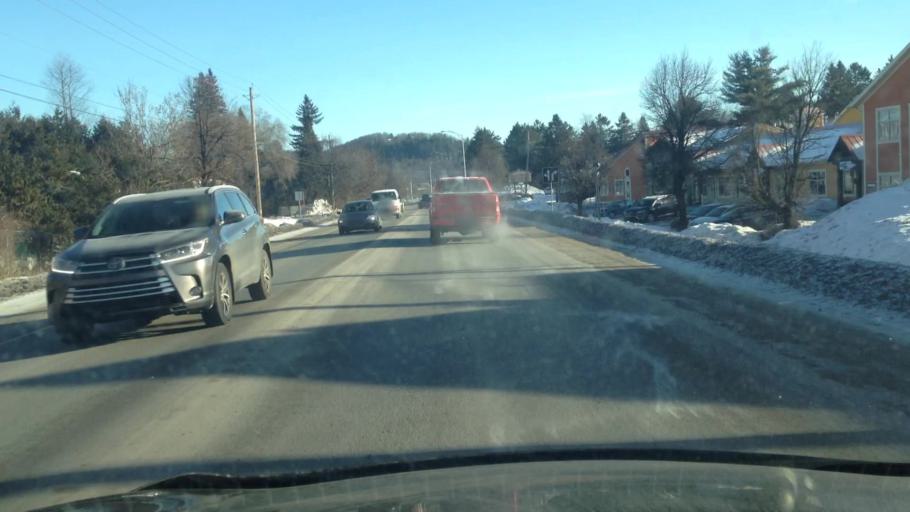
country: CA
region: Quebec
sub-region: Laurentides
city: Saint-Sauveur
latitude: 45.8901
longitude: -74.1625
